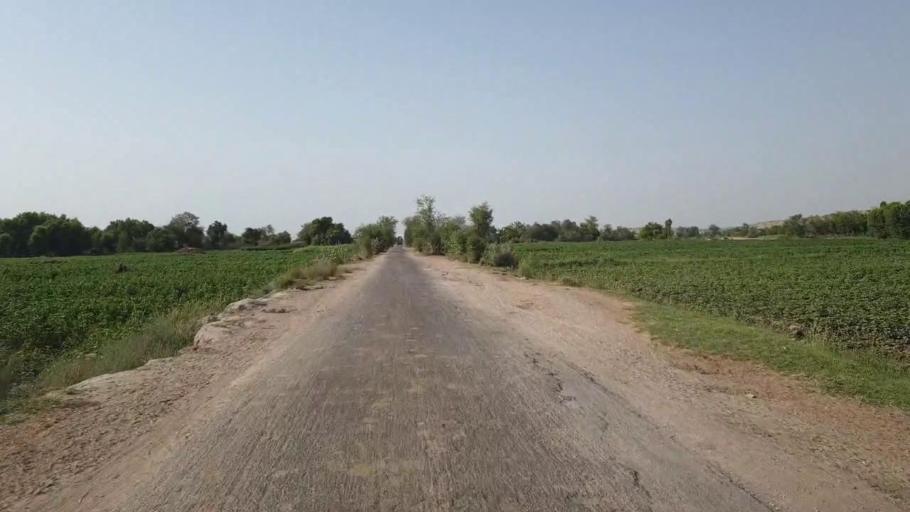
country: PK
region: Sindh
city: Kandiari
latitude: 26.6888
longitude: 68.9645
